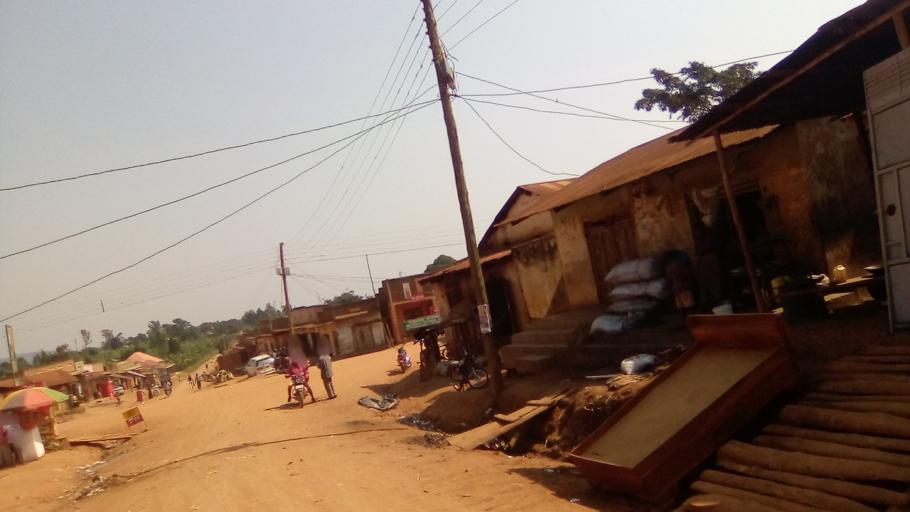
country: UG
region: Central Region
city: Masaka
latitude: -0.2690
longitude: 31.6469
